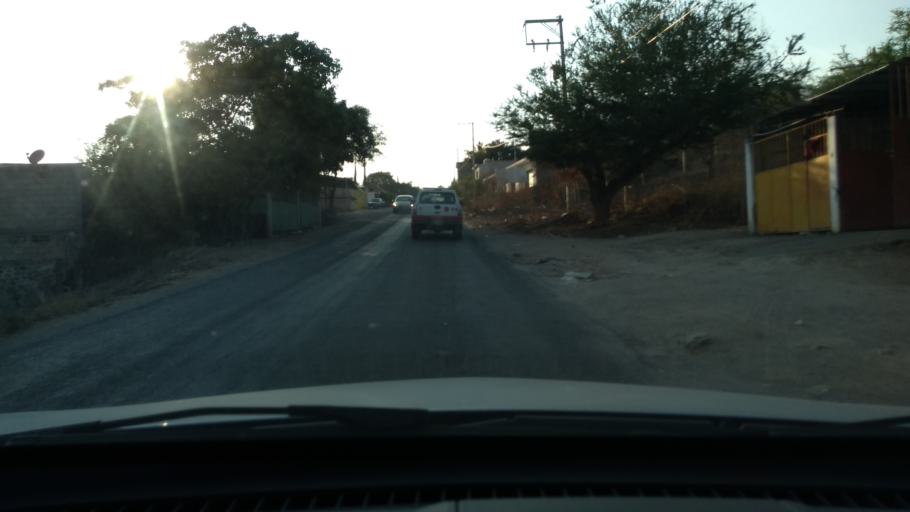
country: MX
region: Morelos
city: Puente de Ixtla
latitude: 18.6148
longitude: -99.3130
